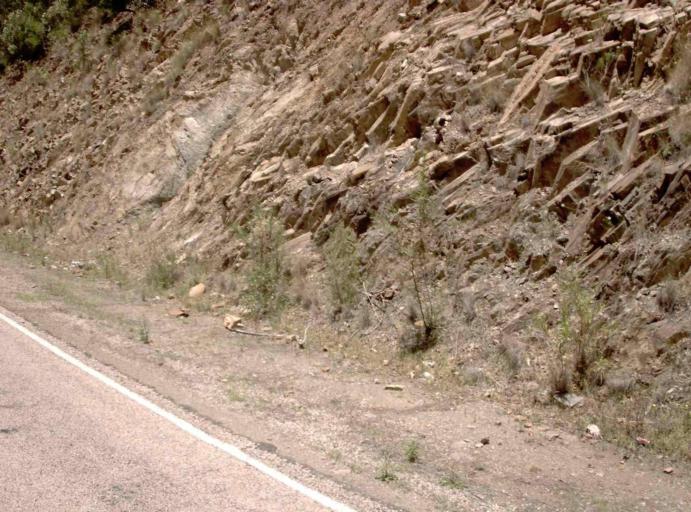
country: AU
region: Victoria
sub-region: East Gippsland
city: Lakes Entrance
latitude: -37.5291
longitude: 147.8525
